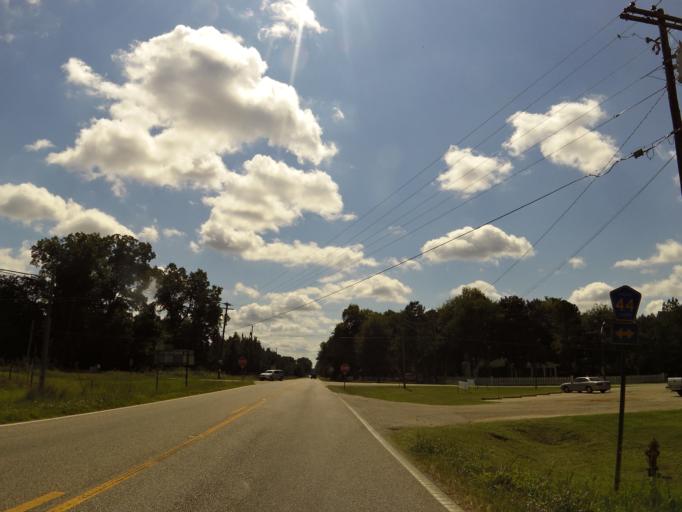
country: US
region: Alabama
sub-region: Dallas County
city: Selma
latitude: 32.4217
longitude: -87.0833
